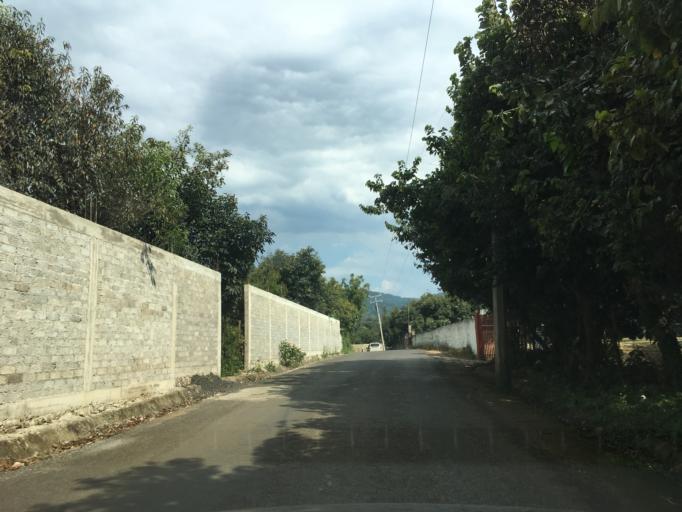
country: MX
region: Michoacan
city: Tingambato
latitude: 19.4998
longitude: -101.8654
